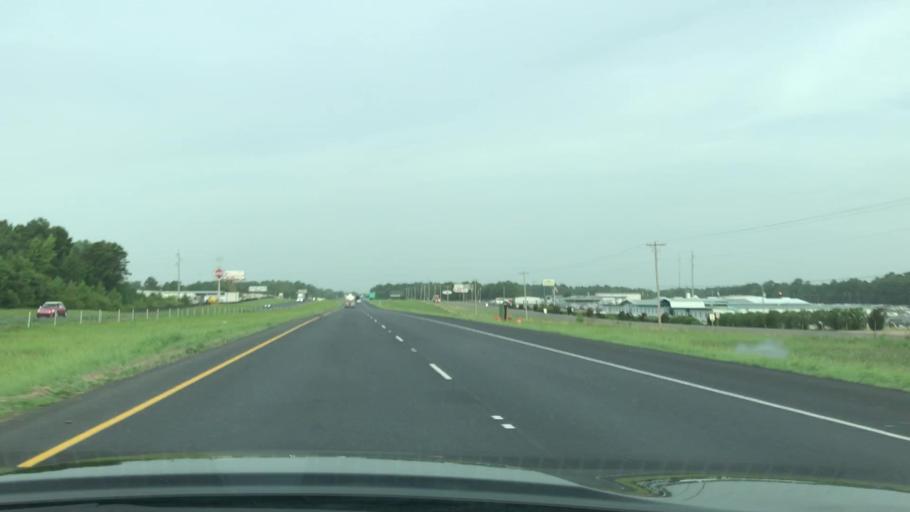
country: US
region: Louisiana
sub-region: Caddo Parish
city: Greenwood
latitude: 32.4455
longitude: -93.9202
